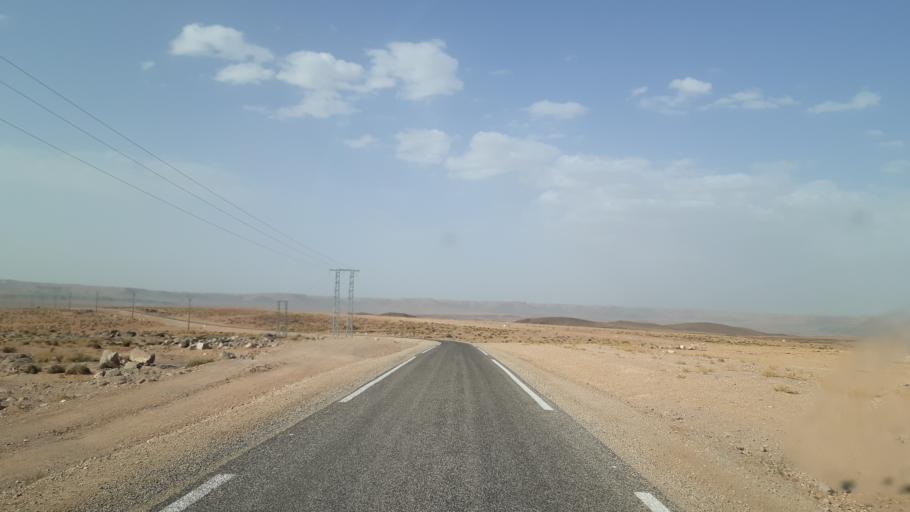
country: MA
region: Meknes-Tafilalet
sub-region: Khenifra
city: Midelt
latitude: 32.8611
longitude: -4.6949
